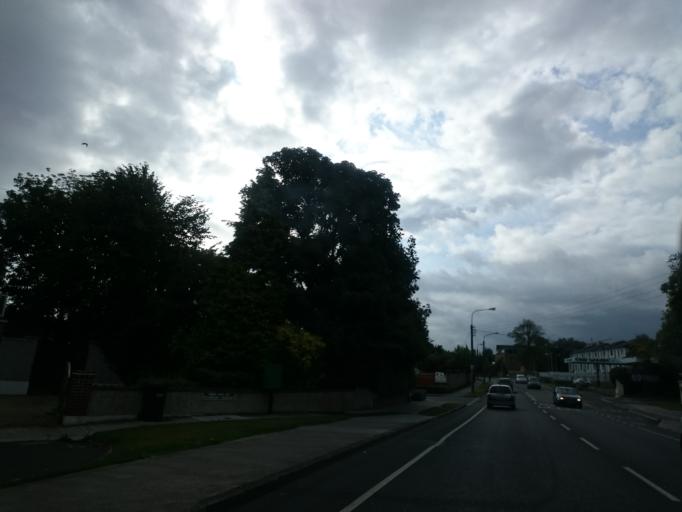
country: IE
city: Clonskeagh
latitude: 53.3048
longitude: -6.2357
